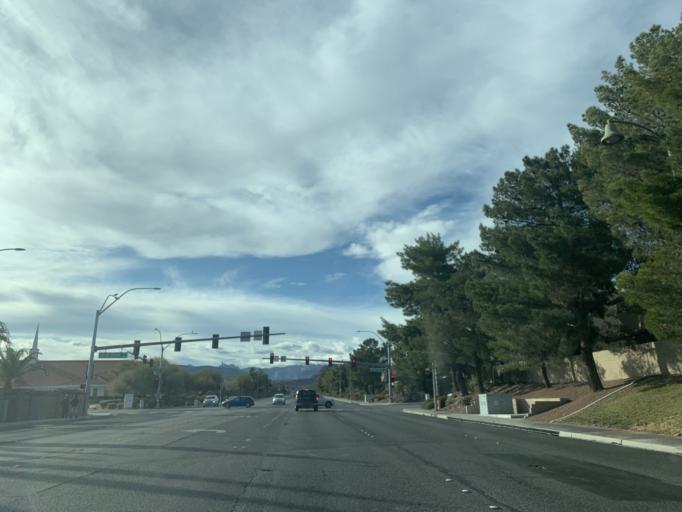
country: US
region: Nevada
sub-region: Clark County
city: Summerlin South
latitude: 36.1299
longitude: -115.3054
